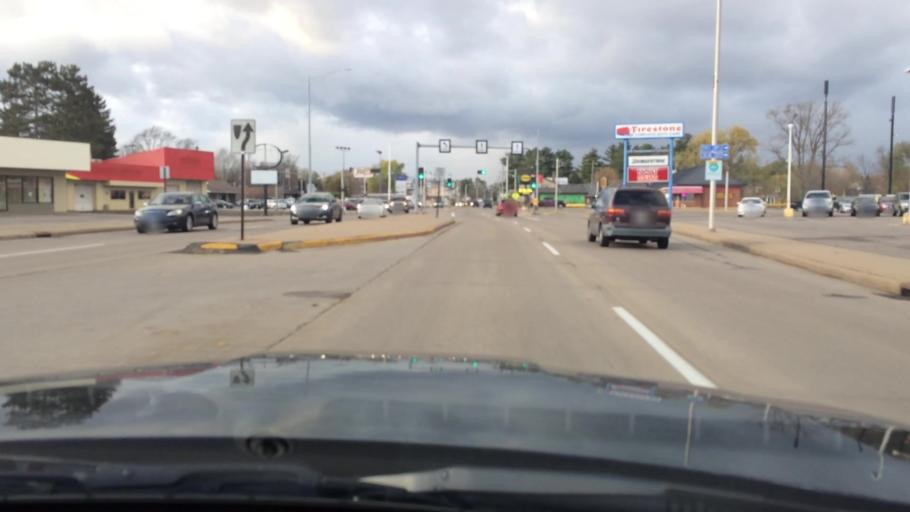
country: US
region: Wisconsin
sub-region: Marathon County
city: Schofield
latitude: 44.9333
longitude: -89.6158
